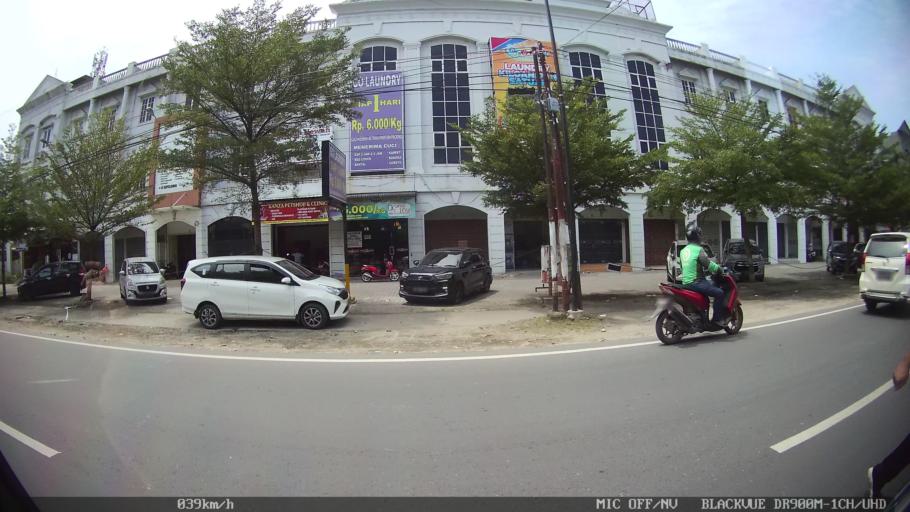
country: ID
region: North Sumatra
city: Sunggal
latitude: 3.5769
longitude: 98.6207
